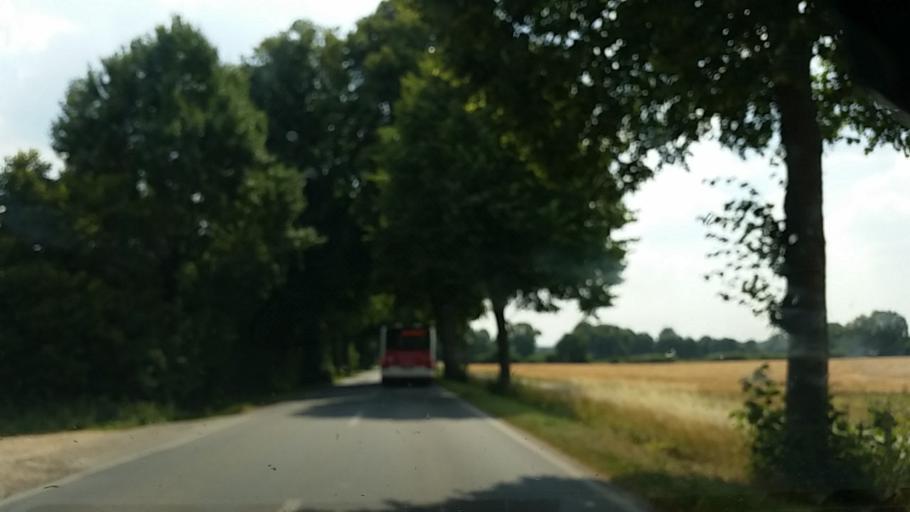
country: DE
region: Schleswig-Holstein
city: Schmilau
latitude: 53.6677
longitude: 10.7688
